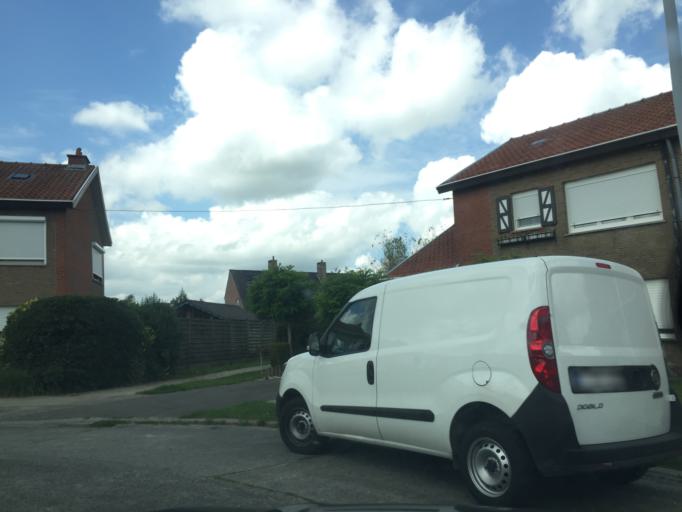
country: BE
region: Flanders
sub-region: Provincie West-Vlaanderen
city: Kortemark
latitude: 51.0317
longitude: 3.0377
